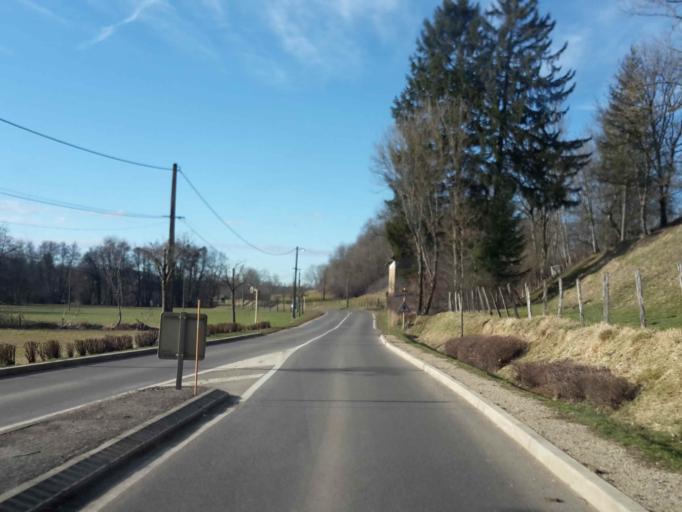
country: FR
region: Franche-Comte
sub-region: Departement du Doubs
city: Vercel-Villedieu-le-Camp
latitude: 47.2336
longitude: 6.3977
